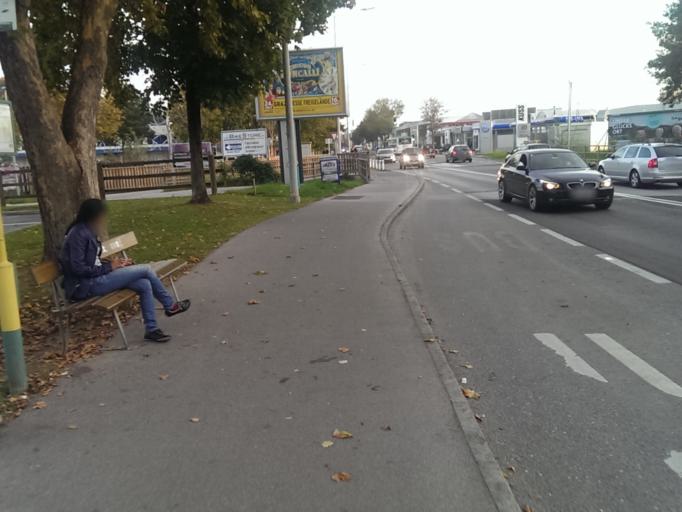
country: AT
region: Styria
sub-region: Graz Stadt
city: Goesting
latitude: 47.1046
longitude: 15.4141
